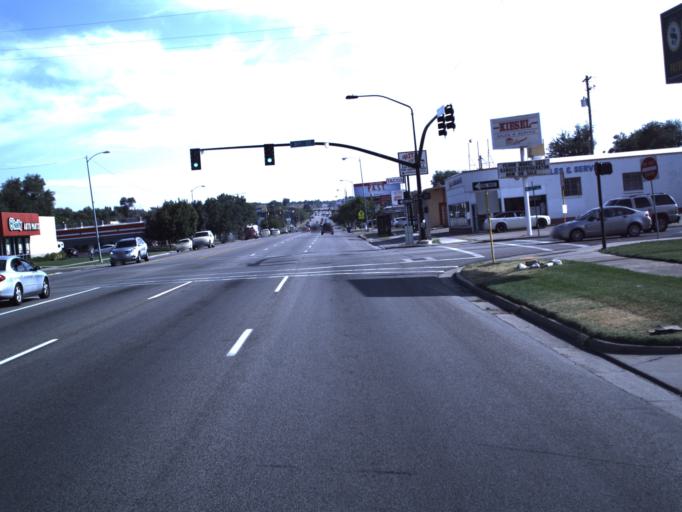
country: US
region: Utah
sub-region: Weber County
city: Ogden
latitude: 41.2086
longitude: -111.9709
